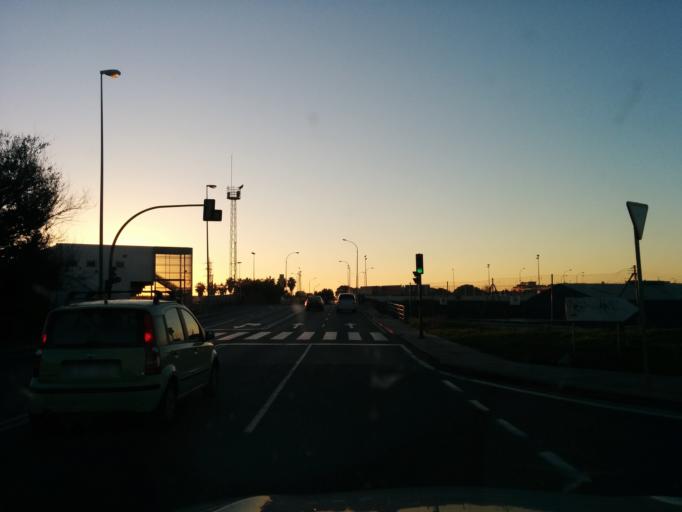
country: ES
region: Andalusia
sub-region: Provincia de Sevilla
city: Sevilla
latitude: 37.3795
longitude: -5.9363
